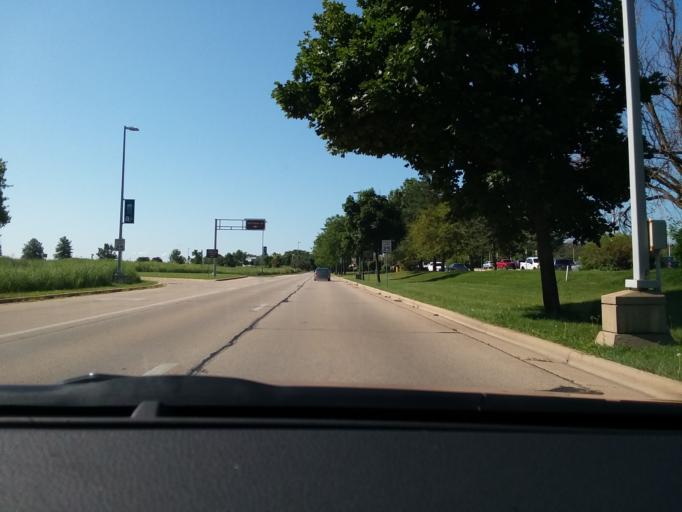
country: US
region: Wisconsin
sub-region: Dane County
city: Maple Bluff
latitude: 43.1325
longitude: -89.3485
